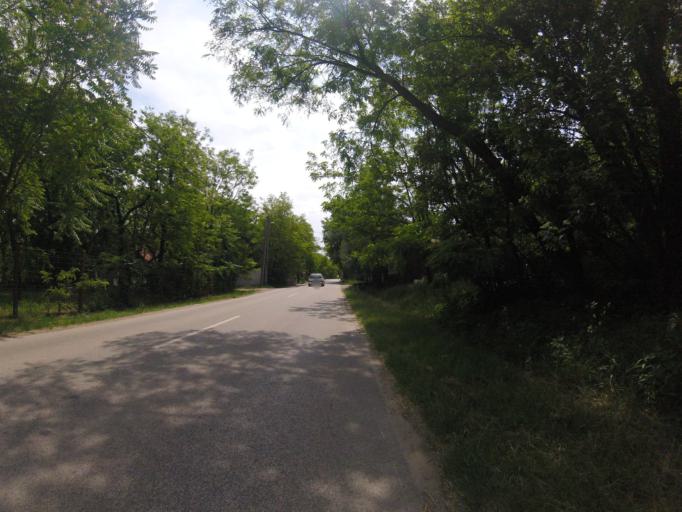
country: HU
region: Pest
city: Tahitotfalu
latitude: 47.7460
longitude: 19.0973
